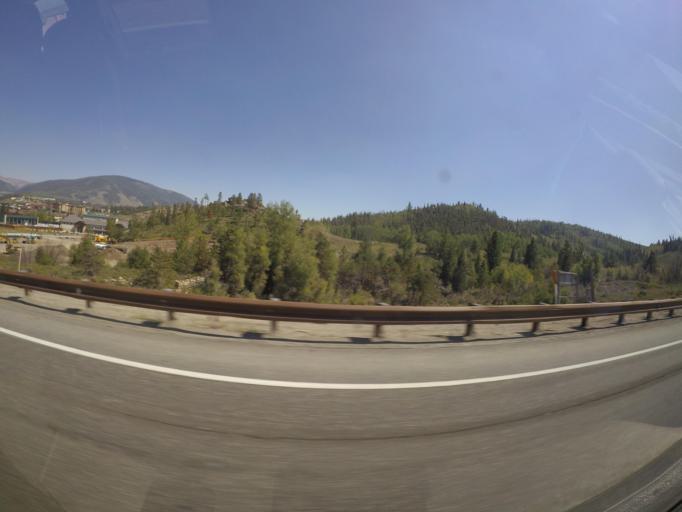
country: US
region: Colorado
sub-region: Summit County
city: Silverthorne
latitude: 39.6245
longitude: -106.0736
